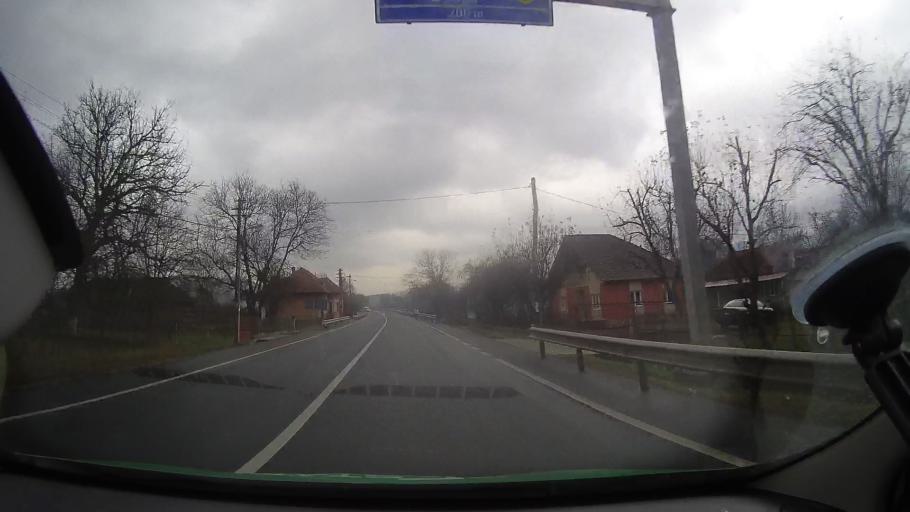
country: RO
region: Hunedoara
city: Vata de Jos
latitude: 46.1907
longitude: 22.6165
